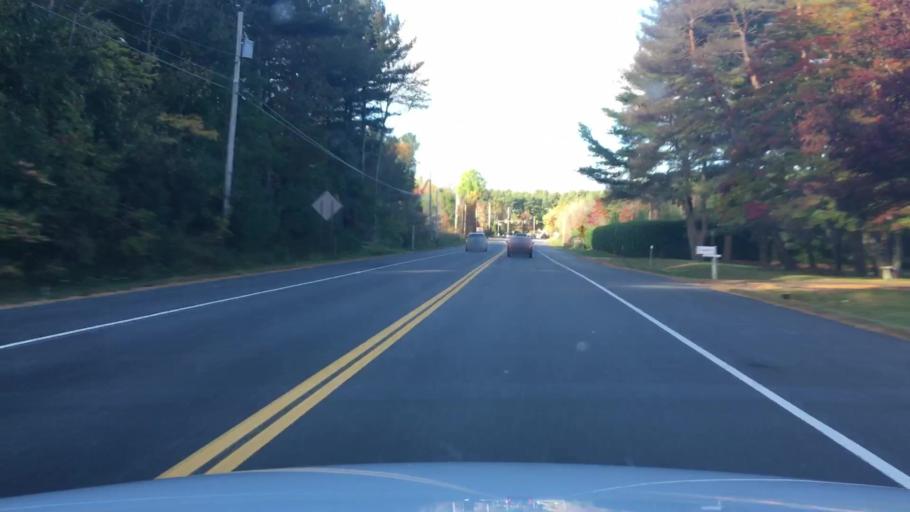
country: US
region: Maine
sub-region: York County
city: Eliot
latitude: 43.1303
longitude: -70.8563
